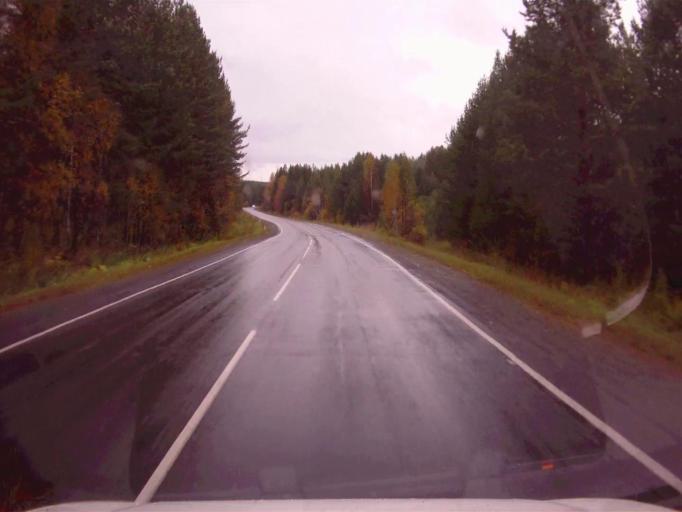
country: RU
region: Chelyabinsk
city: Verkhniy Ufaley
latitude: 56.0108
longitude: 60.3200
